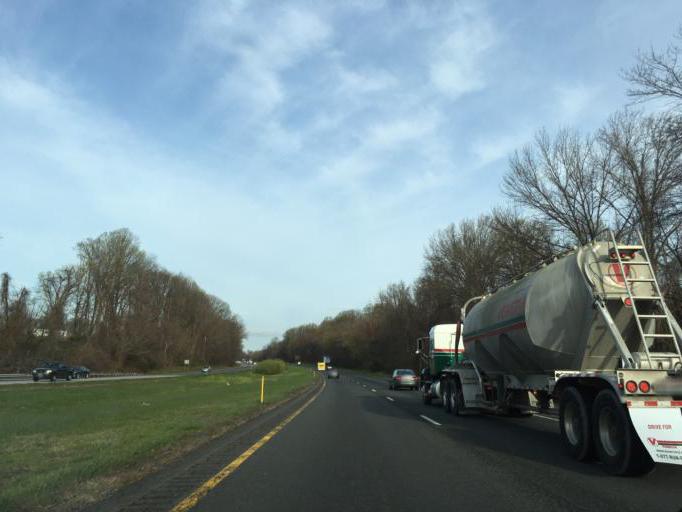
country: US
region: Maryland
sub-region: Howard County
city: Columbia
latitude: 39.3039
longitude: -76.8773
